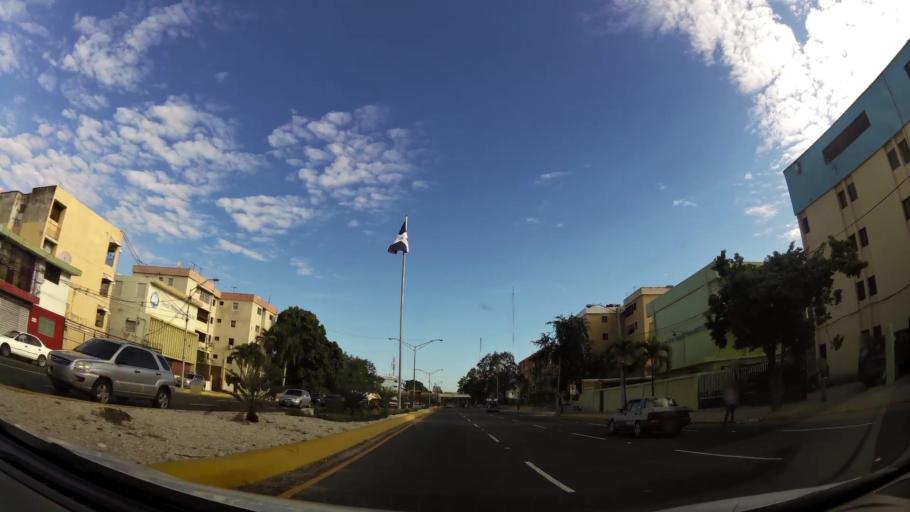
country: DO
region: Nacional
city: San Carlos
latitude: 18.4838
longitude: -69.9061
